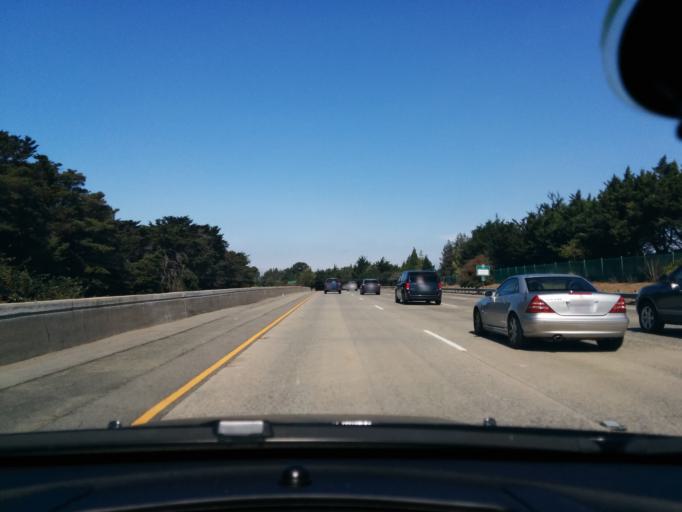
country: US
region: California
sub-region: San Mateo County
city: Hillsborough
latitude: 37.5631
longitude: -122.3858
